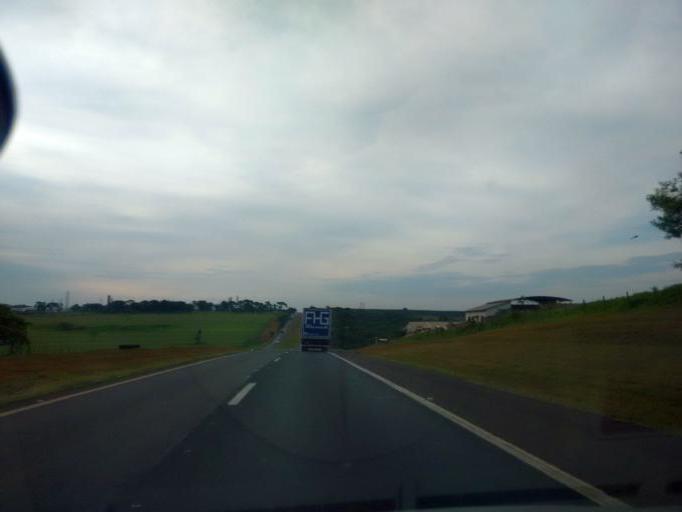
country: BR
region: Sao Paulo
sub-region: Araraquara
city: Araraquara
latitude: -21.7959
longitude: -48.2094
